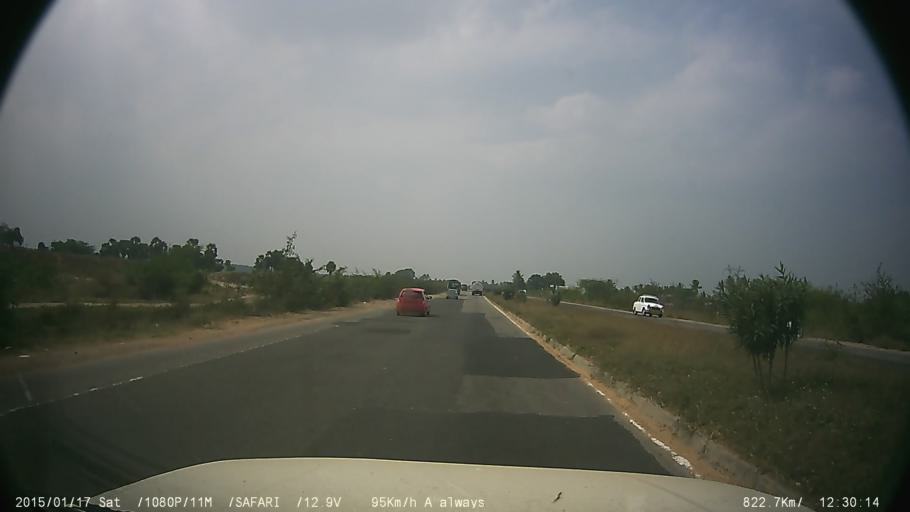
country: IN
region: Tamil Nadu
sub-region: Kancheepuram
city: Kanchipuram
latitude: 12.8744
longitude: 79.6791
